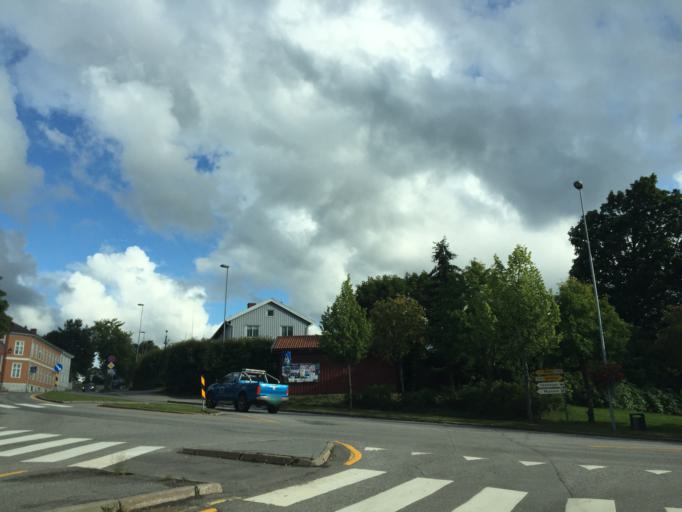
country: NO
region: Hedmark
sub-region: Kongsvinger
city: Kongsvinger
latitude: 60.1952
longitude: 12.0053
